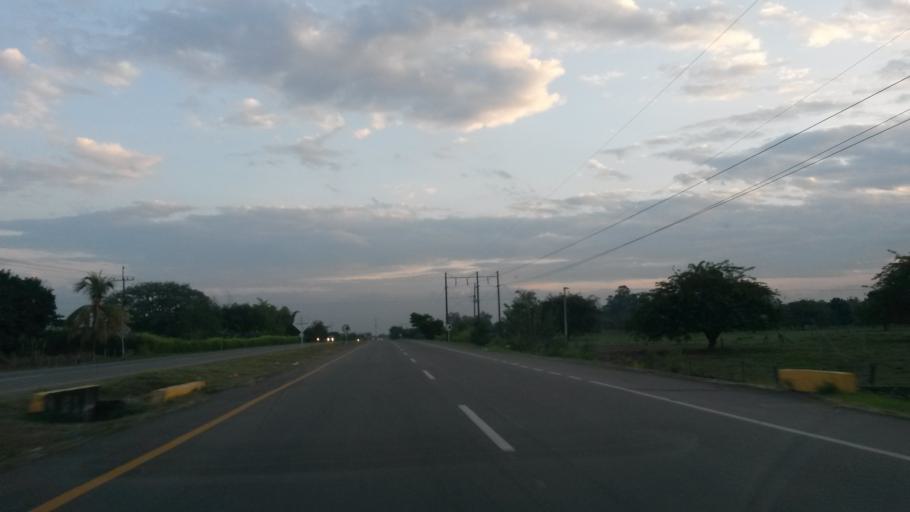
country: CO
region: Cauca
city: Santander de Quilichao
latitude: 3.0591
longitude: -76.4745
